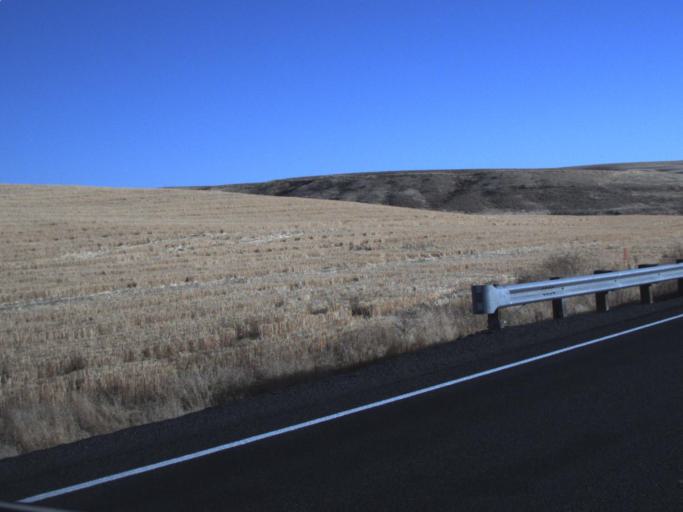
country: US
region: Washington
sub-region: Adams County
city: Ritzville
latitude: 46.7861
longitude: -118.2880
